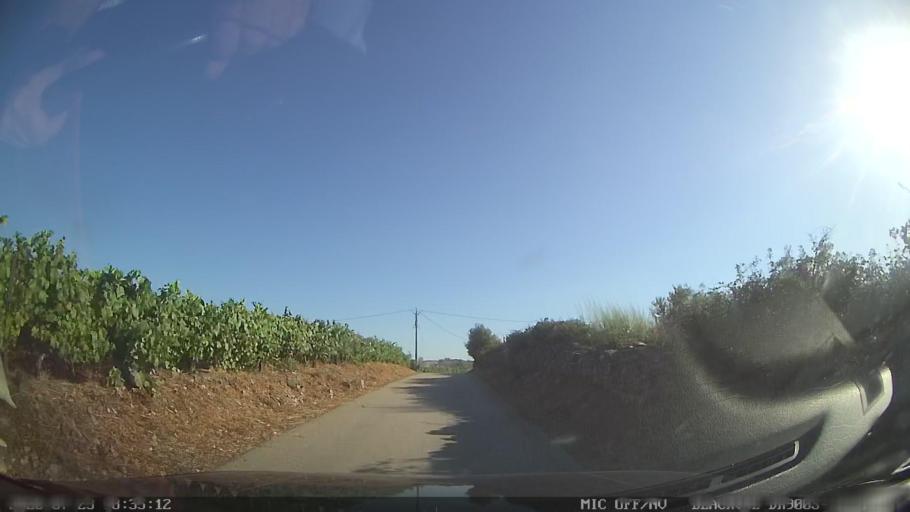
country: PT
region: Viseu
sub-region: Sao Joao da Pesqueira
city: Sao Joao da Pesqueira
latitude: 41.1593
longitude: -7.4170
